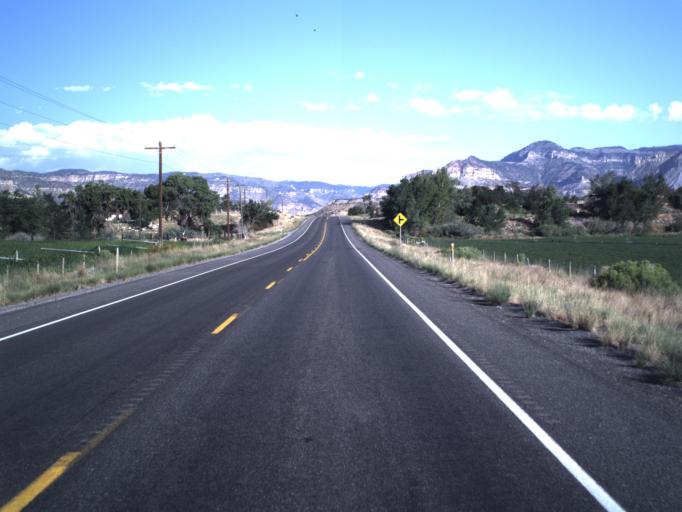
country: US
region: Utah
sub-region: Emery County
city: Huntington
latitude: 39.3483
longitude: -110.9957
